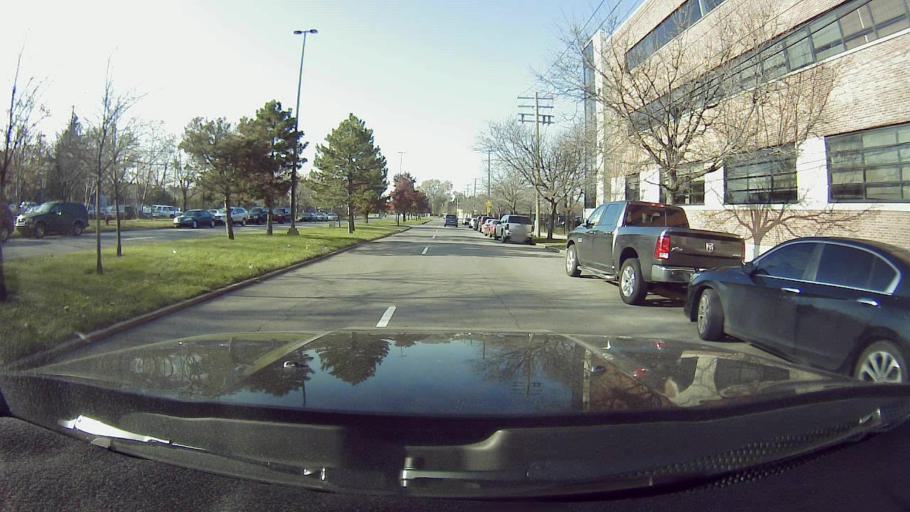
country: US
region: Michigan
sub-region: Wayne County
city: Highland Park
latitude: 42.3991
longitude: -83.1231
